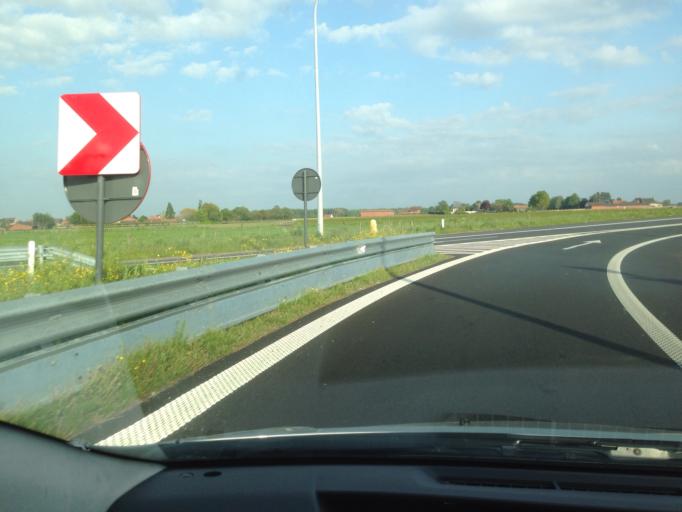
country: BE
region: Flanders
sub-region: Provincie West-Vlaanderen
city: Zedelgem
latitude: 51.1111
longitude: 3.1858
